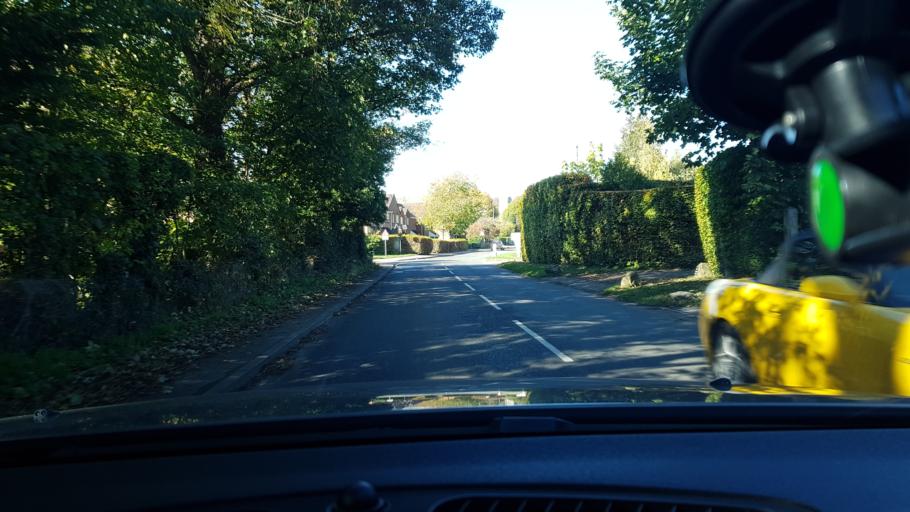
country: GB
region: England
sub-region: Wiltshire
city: Aldbourne
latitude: 51.4764
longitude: -1.6163
